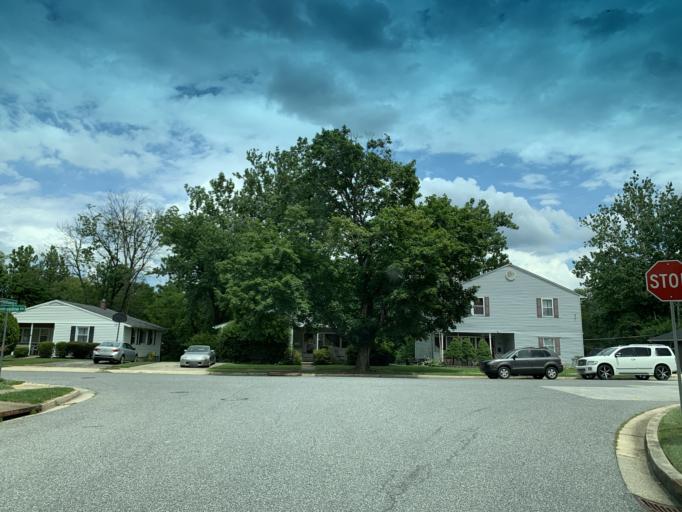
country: US
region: Maryland
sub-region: Baltimore County
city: Timonium
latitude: 39.4416
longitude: -76.6195
